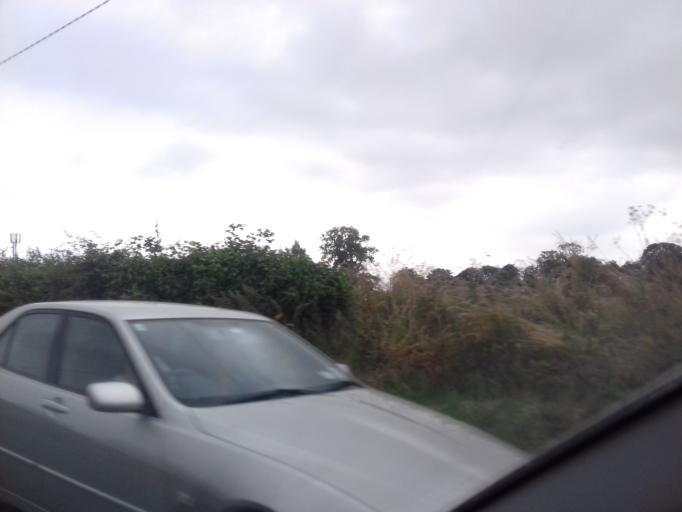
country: IE
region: Leinster
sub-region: Fingal County
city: Swords
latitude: 53.4805
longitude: -6.2345
